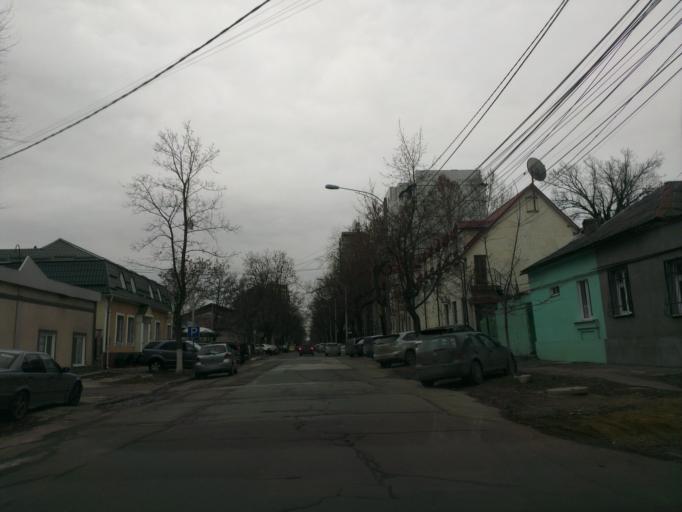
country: MD
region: Chisinau
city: Chisinau
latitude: 47.0292
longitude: 28.8320
